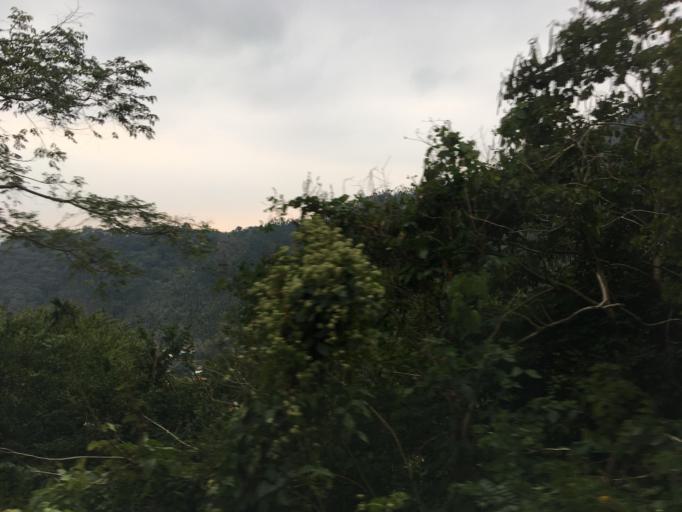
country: TW
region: Taiwan
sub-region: Chiayi
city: Jiayi Shi
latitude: 23.5353
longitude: 120.6058
